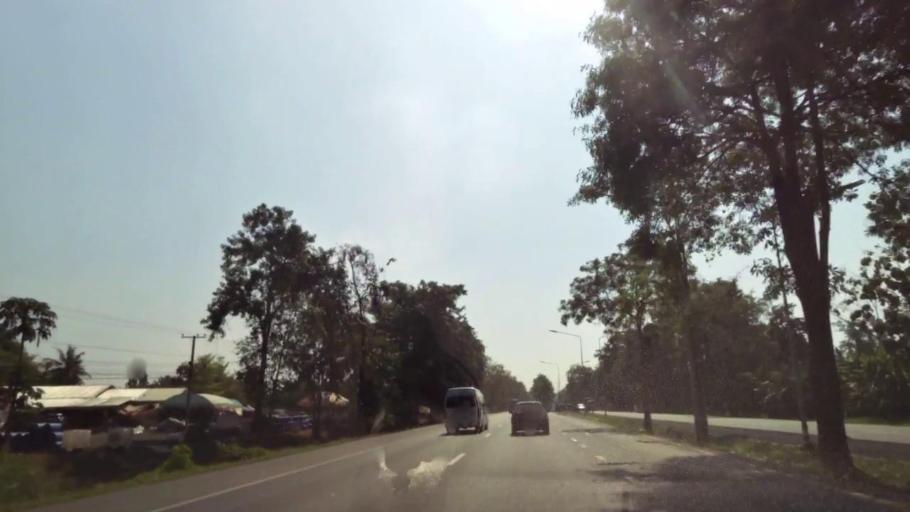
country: TH
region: Phichit
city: Bueng Na Rang
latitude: 16.0642
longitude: 100.1234
